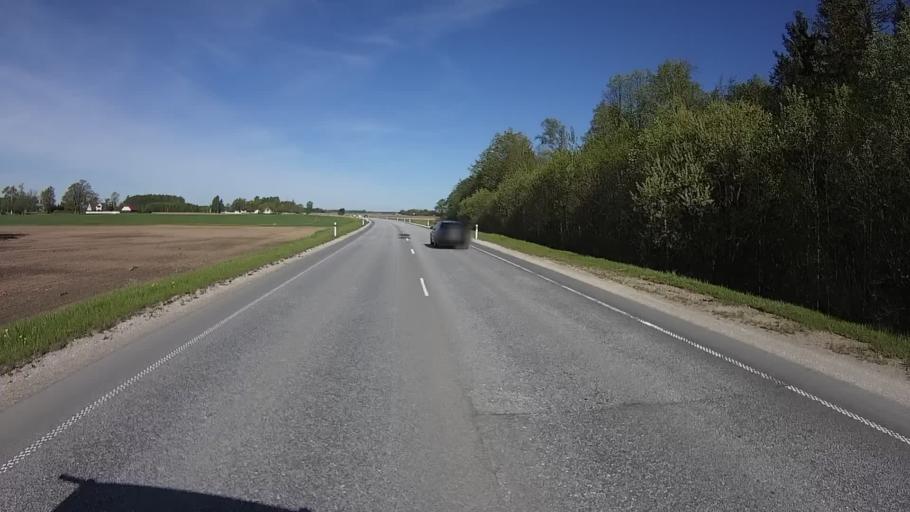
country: EE
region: Tartu
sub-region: Tartu linn
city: Tartu
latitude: 58.3708
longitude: 26.8762
